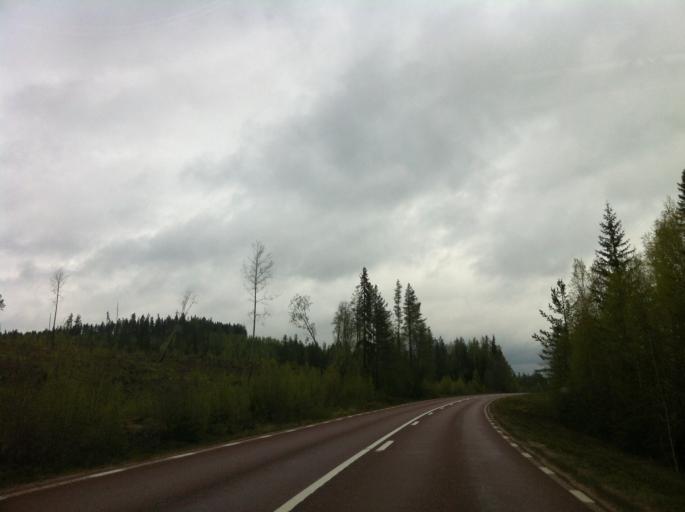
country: SE
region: Jaemtland
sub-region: Harjedalens Kommun
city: Sveg
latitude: 61.8737
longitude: 14.6295
